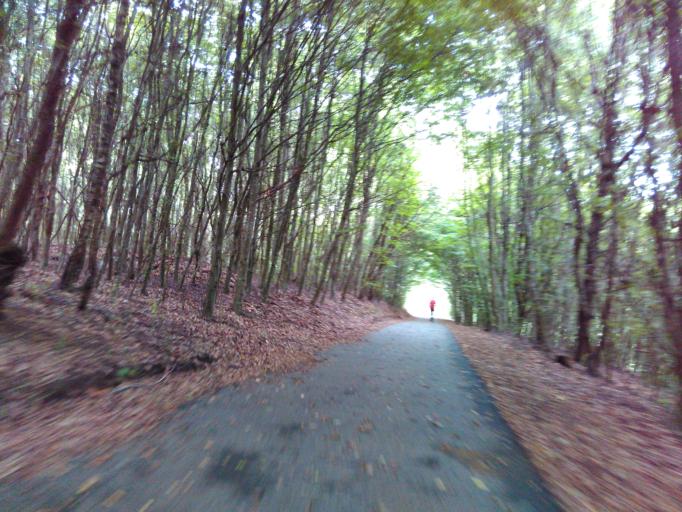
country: LU
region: Luxembourg
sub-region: Canton de Luxembourg
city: Niederanven
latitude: 49.6601
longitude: 6.2274
